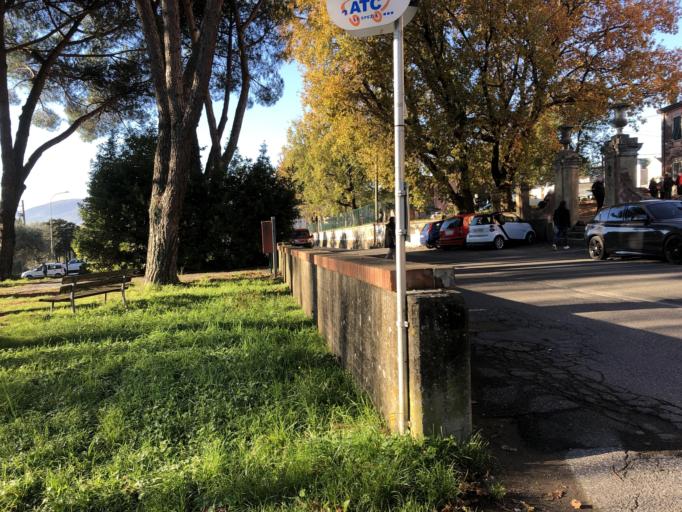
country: IT
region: Tuscany
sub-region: Provincia di Massa-Carrara
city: Borghetto-Melara
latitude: 44.1059
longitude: 9.9864
